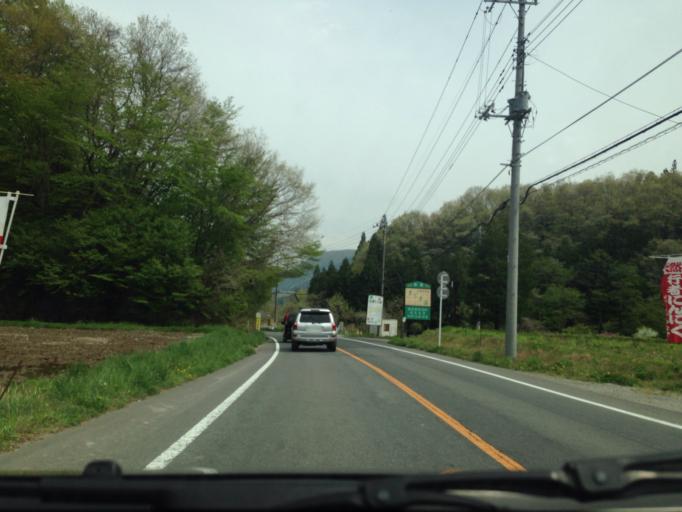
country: JP
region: Tochigi
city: Yaita
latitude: 36.9841
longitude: 139.7809
